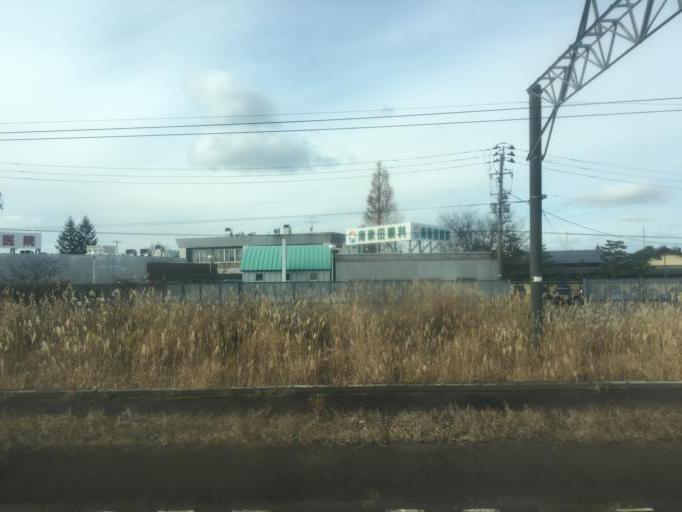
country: JP
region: Akita
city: Tenno
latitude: 39.8703
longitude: 140.0626
